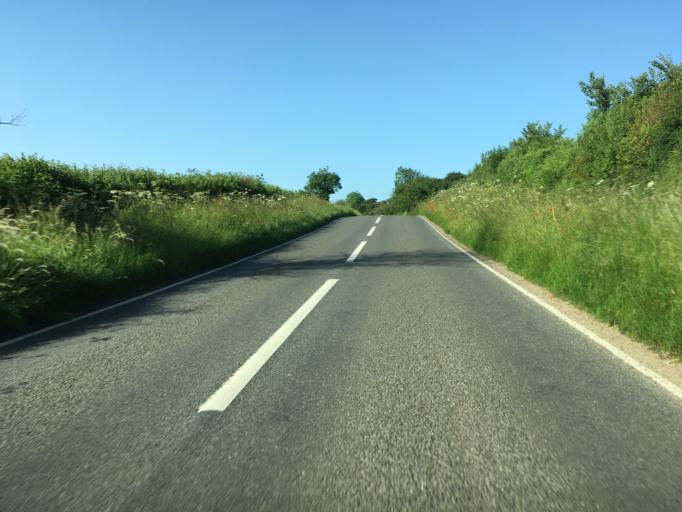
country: GB
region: England
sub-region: Oxfordshire
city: Shipton under Wychwood
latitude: 51.8651
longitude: -1.5437
